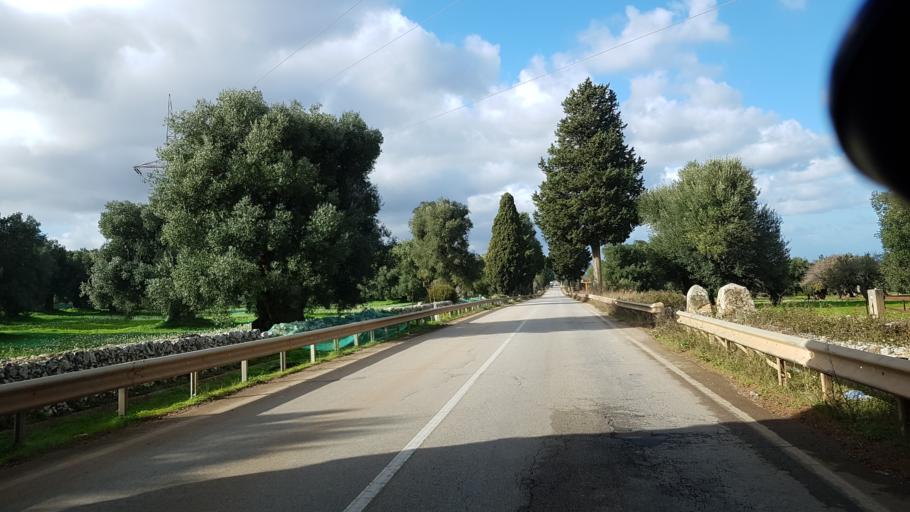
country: IT
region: Apulia
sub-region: Provincia di Brindisi
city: Ostuni
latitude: 40.7528
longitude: 17.5461
